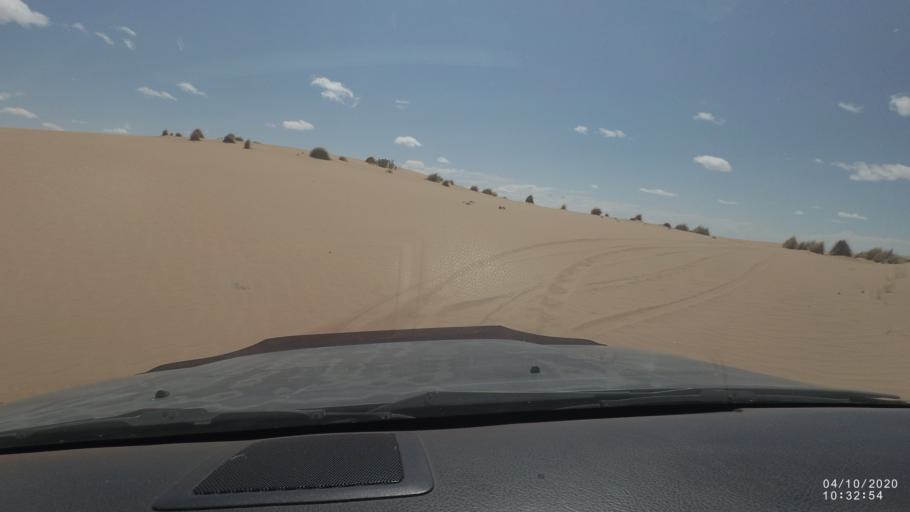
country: BO
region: Oruro
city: Poopo
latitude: -18.7044
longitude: -67.4813
